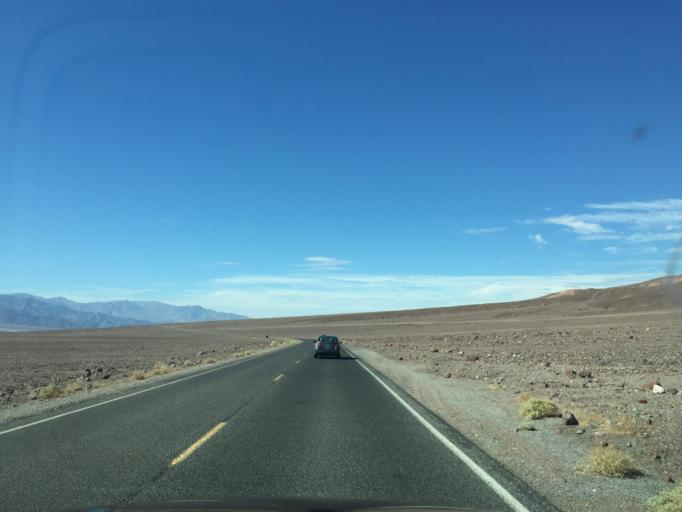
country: US
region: Nevada
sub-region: Nye County
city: Beatty
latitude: 36.2678
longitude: -116.7851
